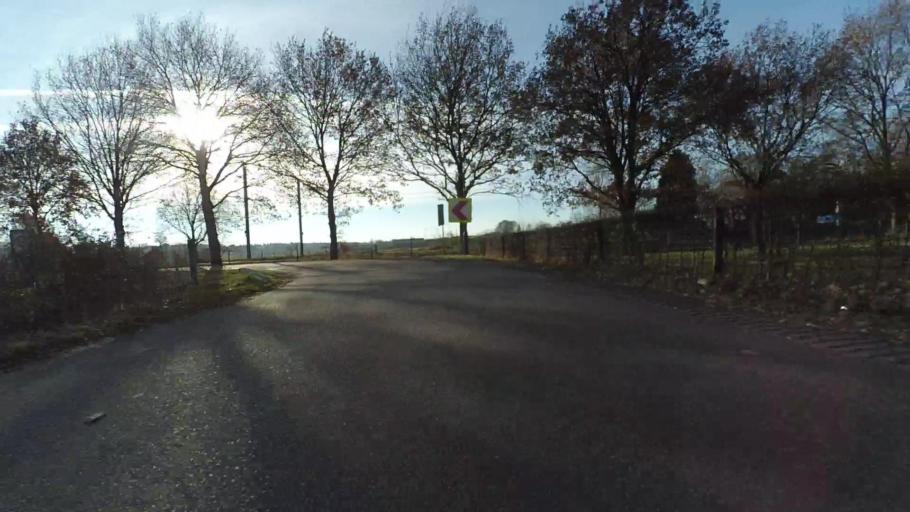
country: NL
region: Utrecht
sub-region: Gemeente Utrechtse Heuvelrug
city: Overberg
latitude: 52.0373
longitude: 5.5030
